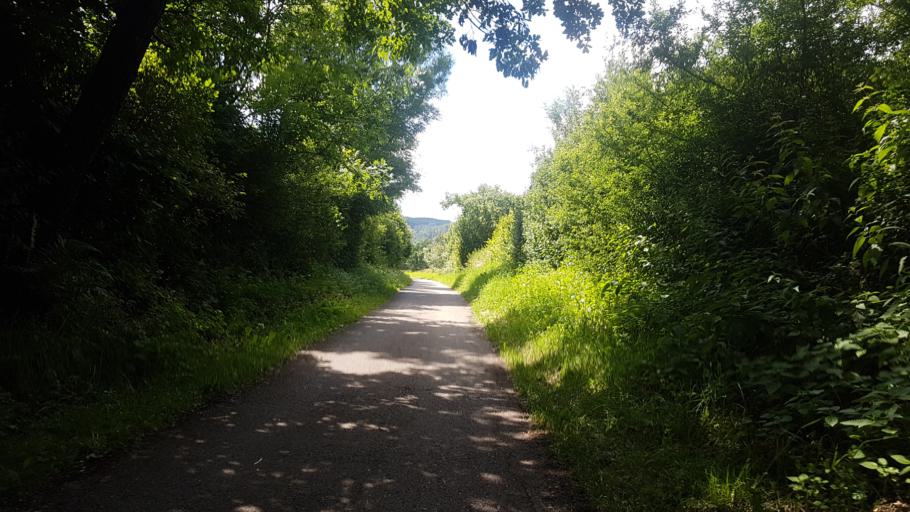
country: DE
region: Bavaria
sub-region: Regierungsbezirk Mittelfranken
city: Pappenheim
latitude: 48.9225
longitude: 10.9794
